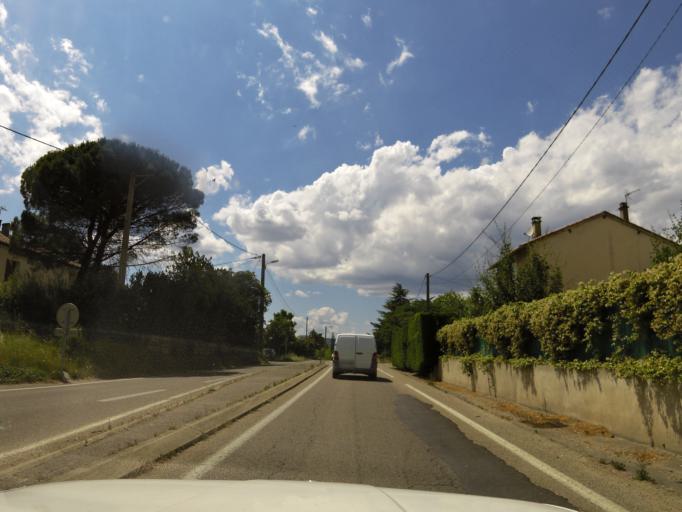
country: FR
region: Languedoc-Roussillon
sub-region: Departement du Gard
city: Saint-Privat-des-Vieux
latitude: 44.1298
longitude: 4.1304
